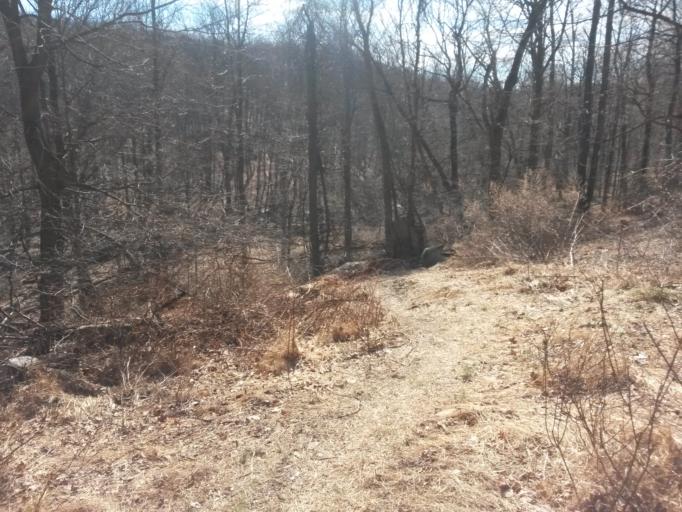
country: US
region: New York
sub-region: Westchester County
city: Yorktown Heights
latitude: 41.2526
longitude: -73.7716
